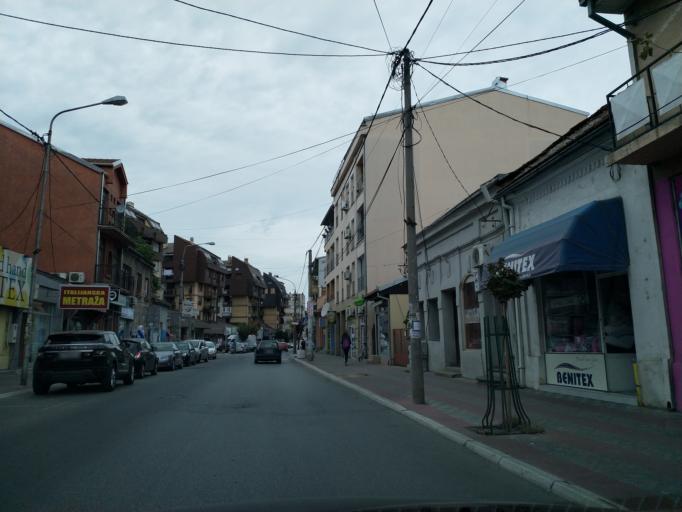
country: RS
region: Central Serbia
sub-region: Pomoravski Okrug
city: Jagodina
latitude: 43.9811
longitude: 21.2571
